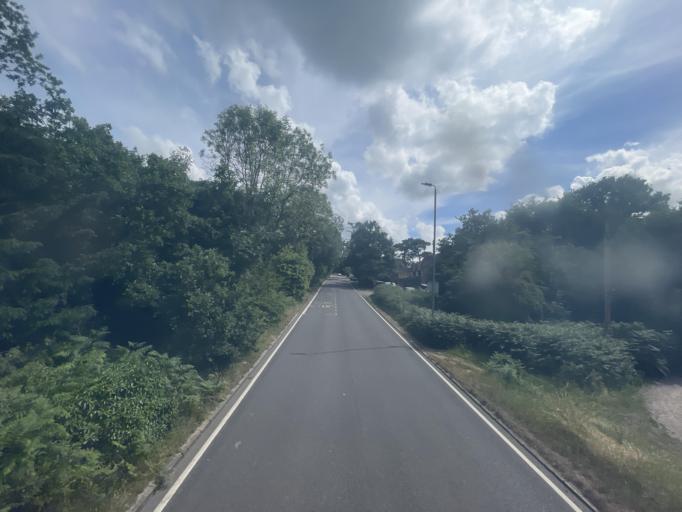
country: GB
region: England
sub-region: Kent
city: Biggin Hill
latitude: 51.3570
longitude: 0.0322
